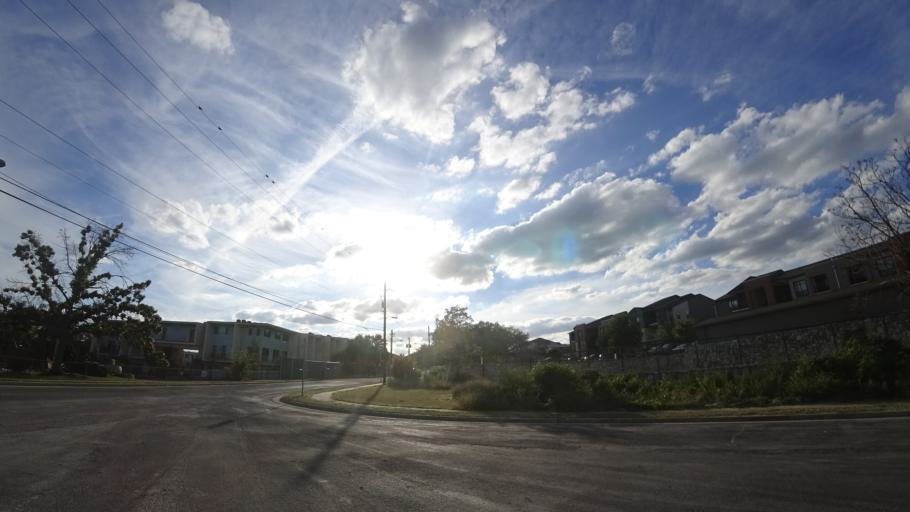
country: US
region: Texas
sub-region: Travis County
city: Onion Creek
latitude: 30.1975
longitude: -97.7708
